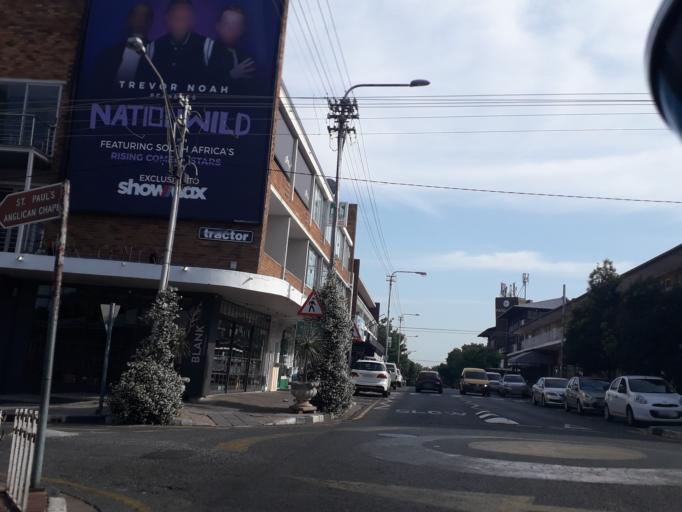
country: ZA
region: Gauteng
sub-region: City of Johannesburg Metropolitan Municipality
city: Johannesburg
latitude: -26.1391
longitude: 28.0176
